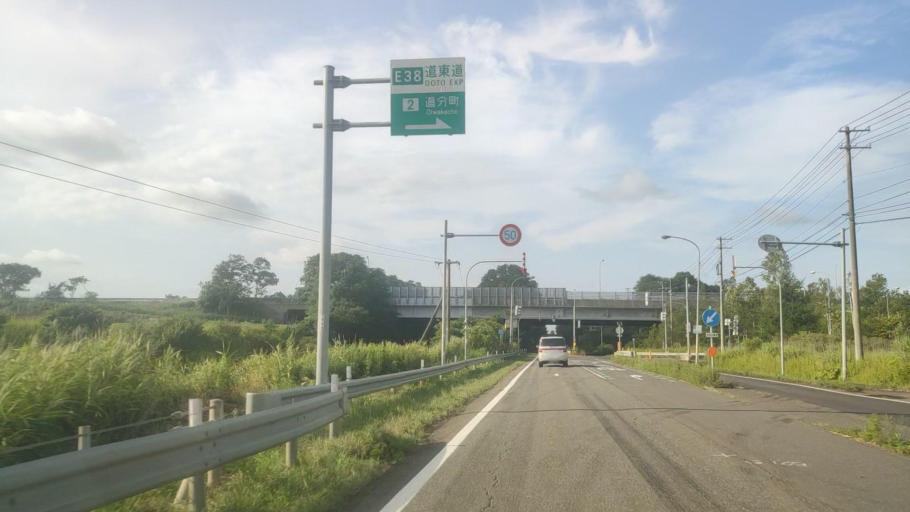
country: JP
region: Hokkaido
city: Chitose
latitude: 42.8917
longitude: 141.8129
